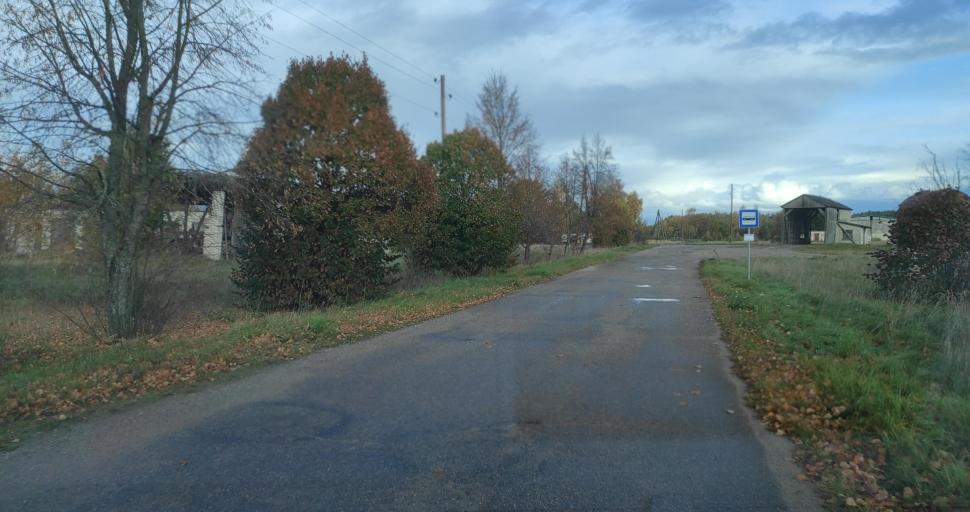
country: LV
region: Skrunda
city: Skrunda
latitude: 56.6840
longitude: 22.0482
